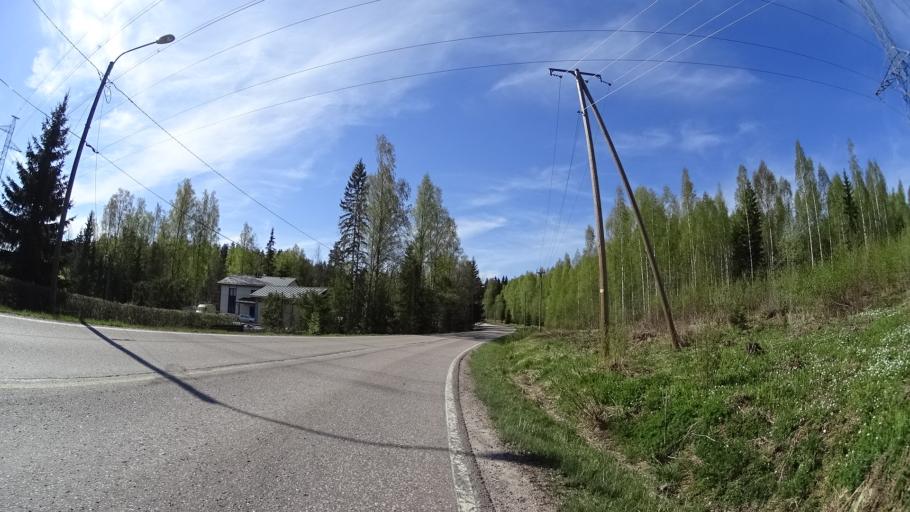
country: FI
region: Uusimaa
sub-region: Helsinki
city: Nurmijaervi
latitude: 60.3844
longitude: 24.8372
